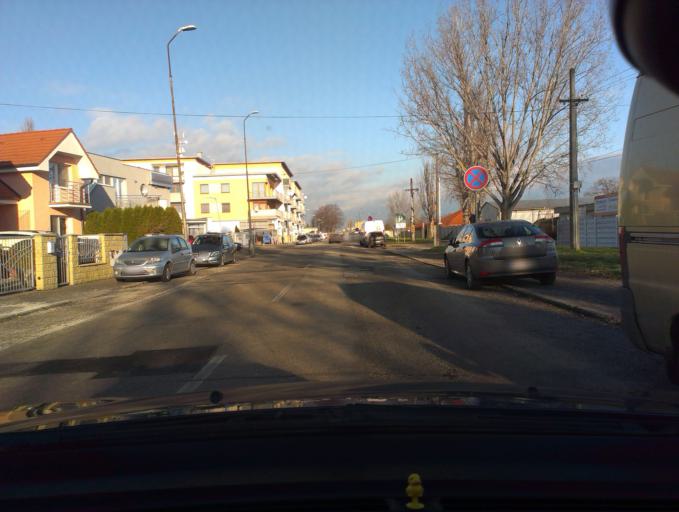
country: SK
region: Trnavsky
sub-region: Okres Trnava
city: Piestany
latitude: 48.6059
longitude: 17.8340
